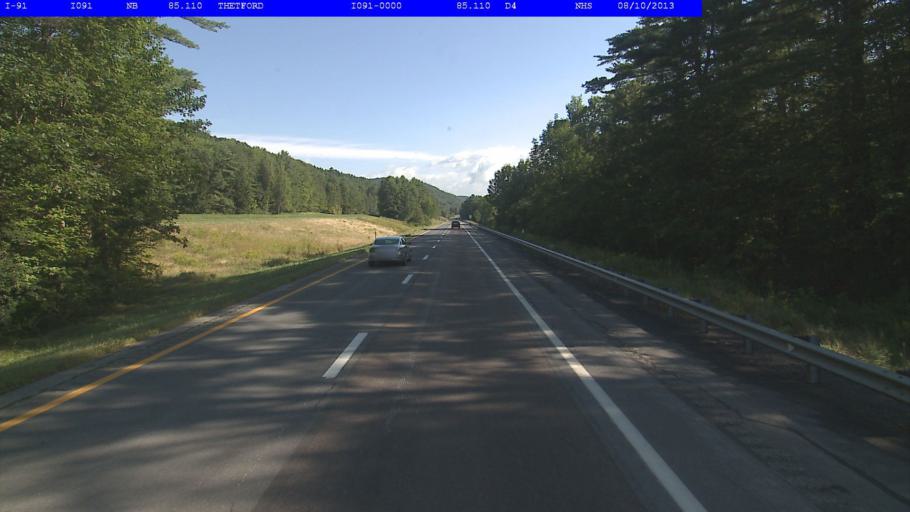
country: US
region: New Hampshire
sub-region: Grafton County
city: Lyme
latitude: 43.8244
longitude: -72.2093
